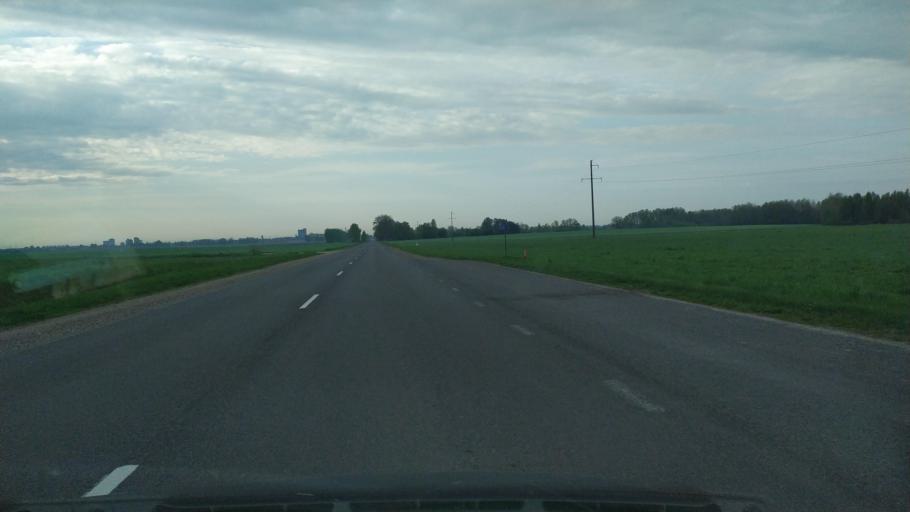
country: BY
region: Brest
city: Zhabinka
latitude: 52.2275
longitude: 23.9877
